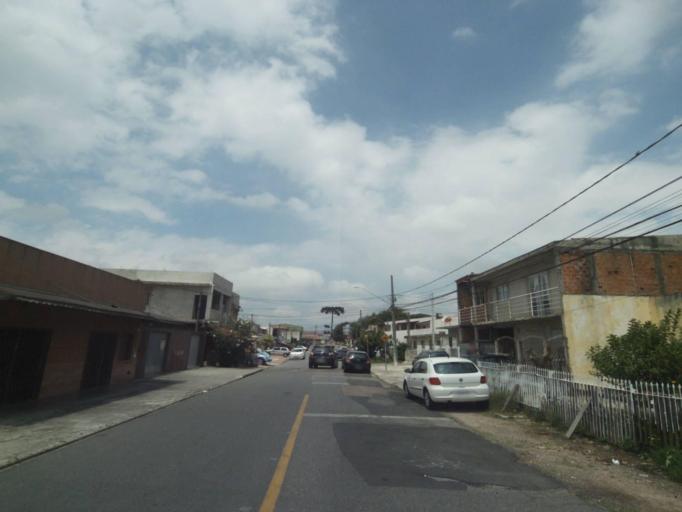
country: BR
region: Parana
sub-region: Curitiba
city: Curitiba
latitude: -25.4780
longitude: -49.3413
